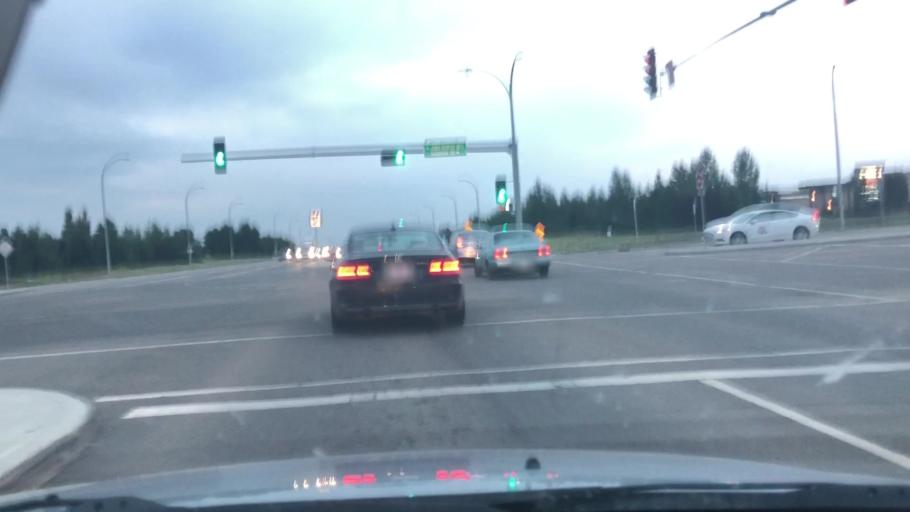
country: CA
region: Alberta
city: St. Albert
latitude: 53.5122
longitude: -113.6781
